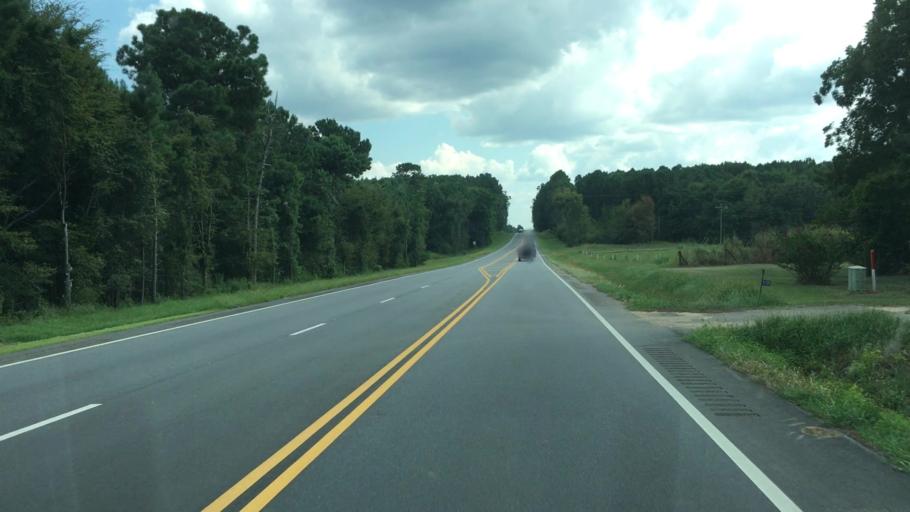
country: US
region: Georgia
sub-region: Putnam County
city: Jefferson
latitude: 33.4653
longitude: -83.4148
